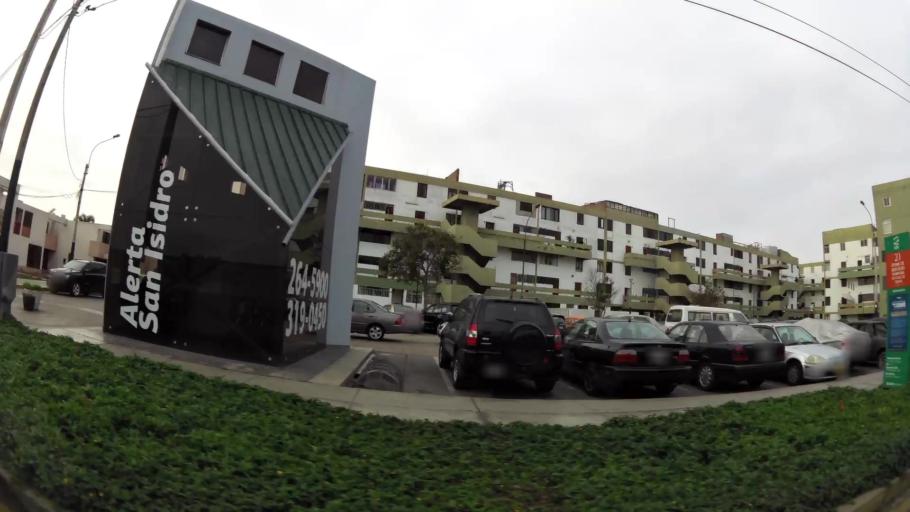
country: PE
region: Lima
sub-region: Lima
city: San Isidro
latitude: -12.1081
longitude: -77.0495
